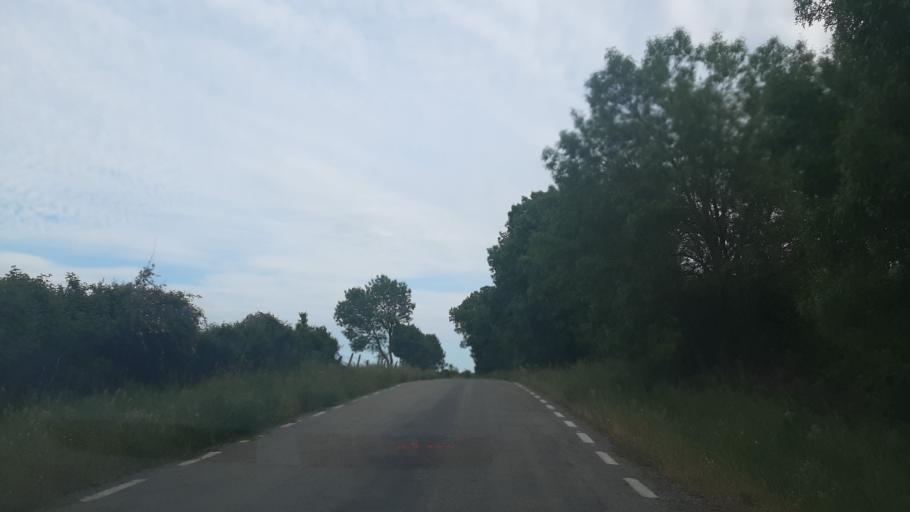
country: ES
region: Castille and Leon
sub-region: Provincia de Salamanca
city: Gallegos de Arganan
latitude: 40.6388
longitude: -6.7284
